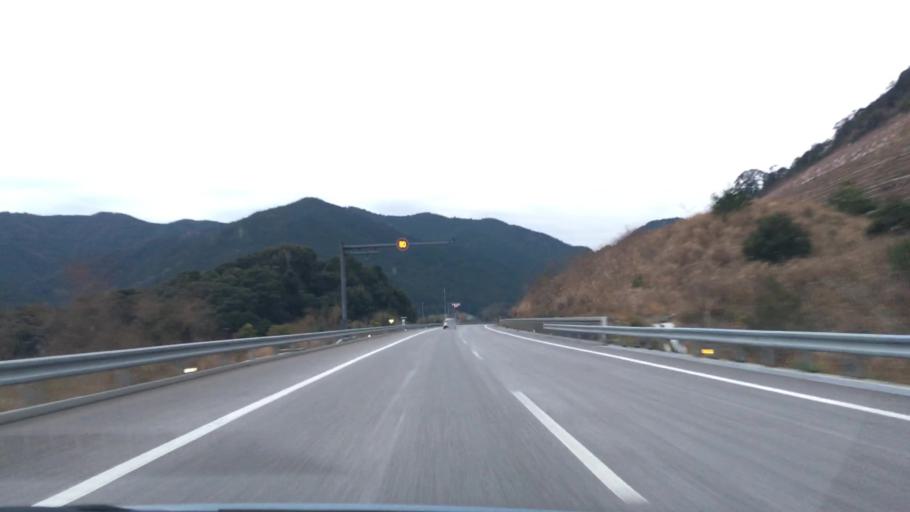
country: JP
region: Aichi
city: Shinshiro
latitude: 34.8437
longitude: 137.6075
